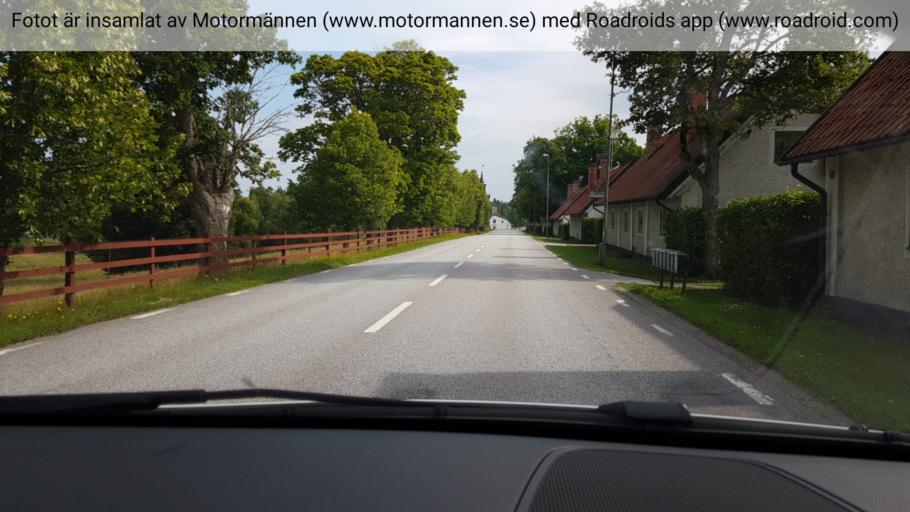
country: SE
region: Uppsala
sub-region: Osthammars Kommun
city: Anneberg
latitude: 60.1852
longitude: 18.3947
